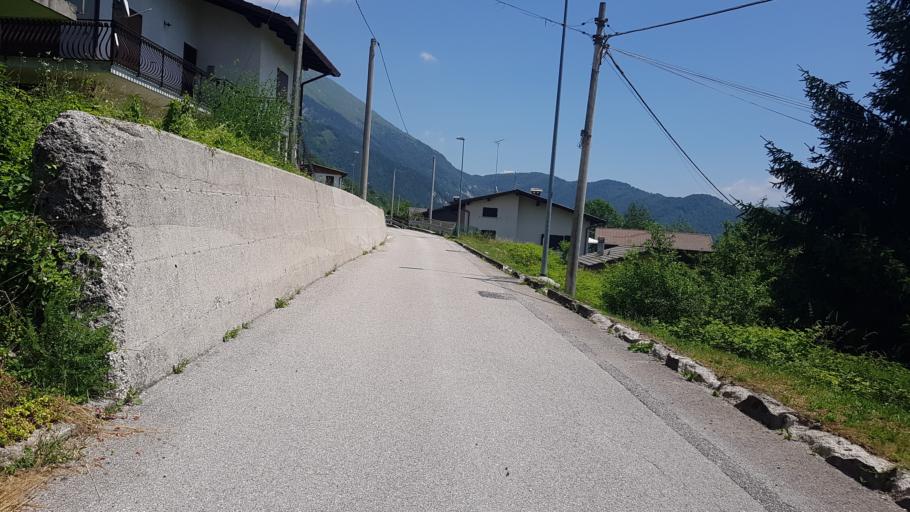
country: IT
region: Friuli Venezia Giulia
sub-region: Provincia di Udine
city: Taipana
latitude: 46.2736
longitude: 13.3126
